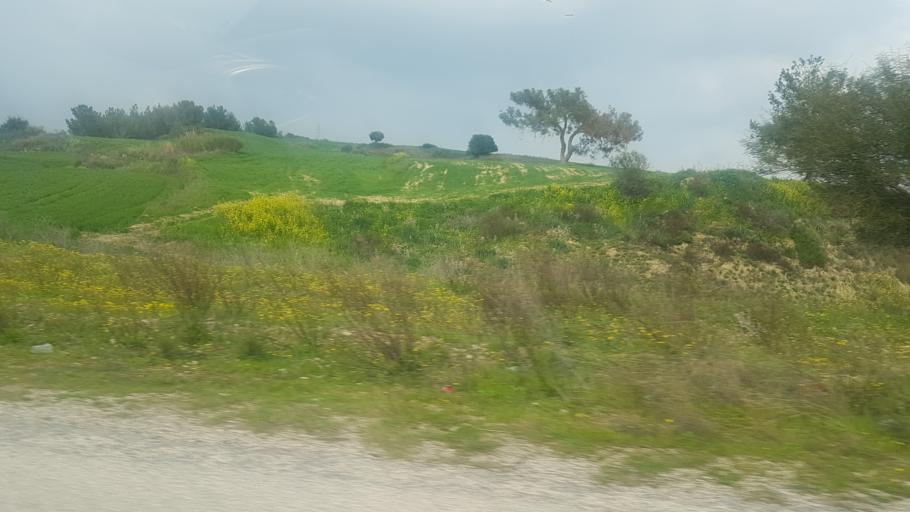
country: TR
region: Adana
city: Seyhan
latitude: 37.0453
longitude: 35.1813
